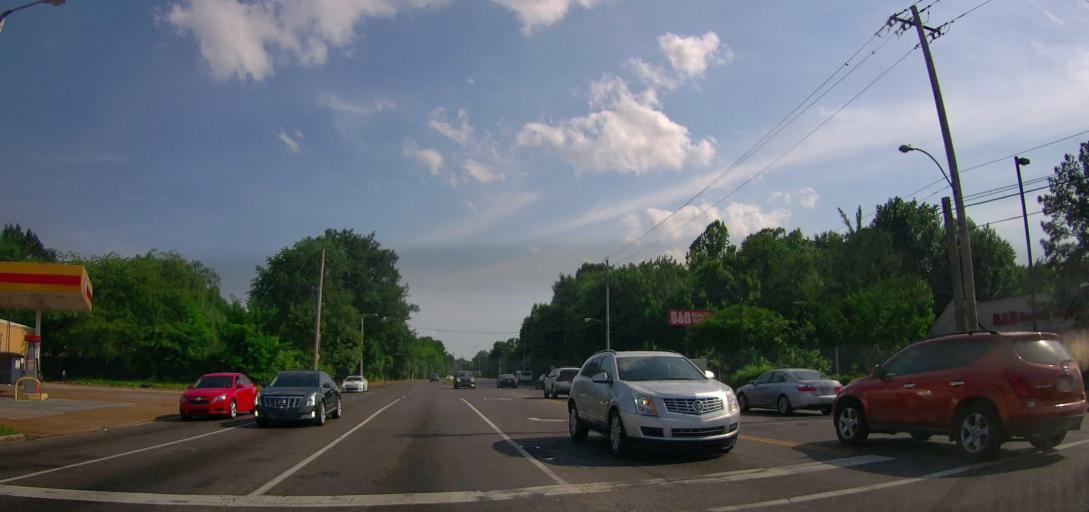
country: US
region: Tennessee
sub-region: Shelby County
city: Germantown
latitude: 35.0349
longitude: -89.8476
